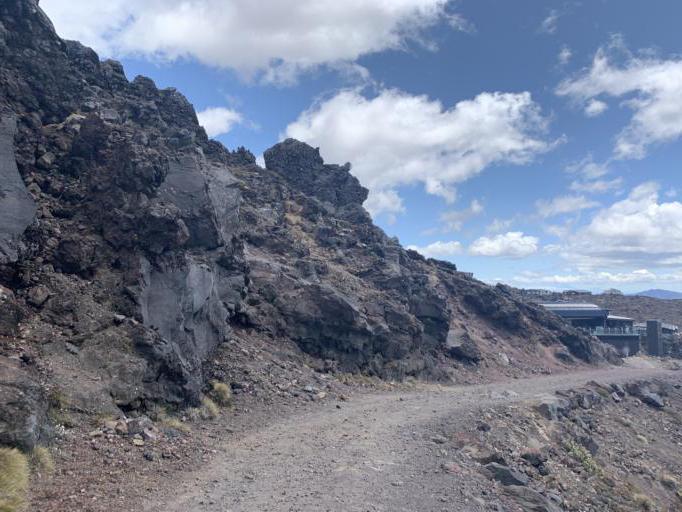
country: NZ
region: Manawatu-Wanganui
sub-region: Ruapehu District
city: Waiouru
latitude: -39.2369
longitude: 175.5593
